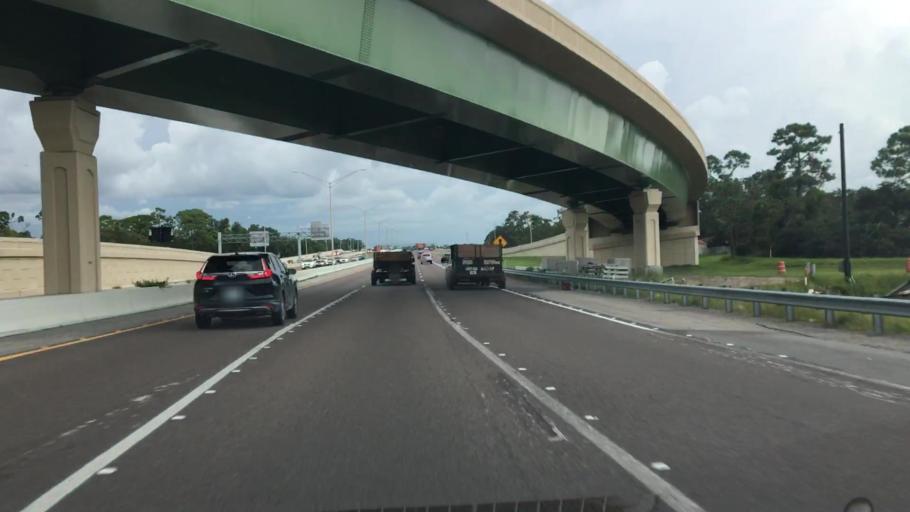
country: US
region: Florida
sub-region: Orange County
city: Union Park
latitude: 28.5498
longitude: -81.2605
